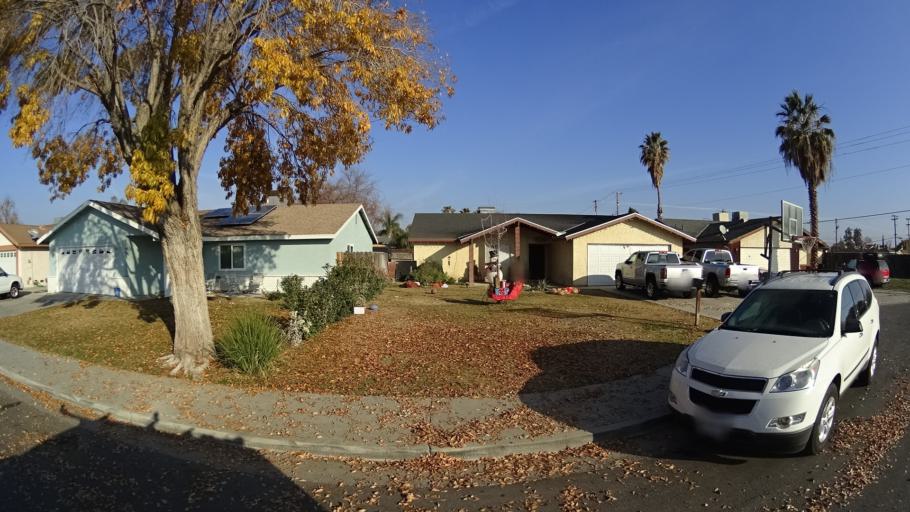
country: US
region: California
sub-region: Kern County
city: Greenfield
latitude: 35.3022
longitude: -119.0218
